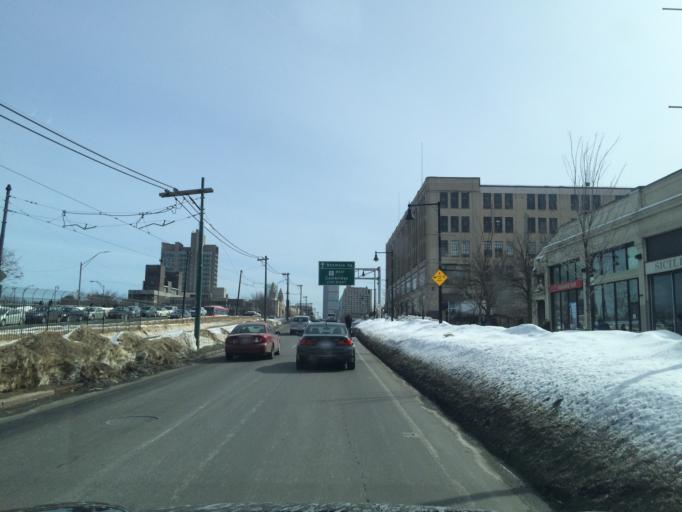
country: US
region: Massachusetts
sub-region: Norfolk County
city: Brookline
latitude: 42.3507
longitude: -71.1132
